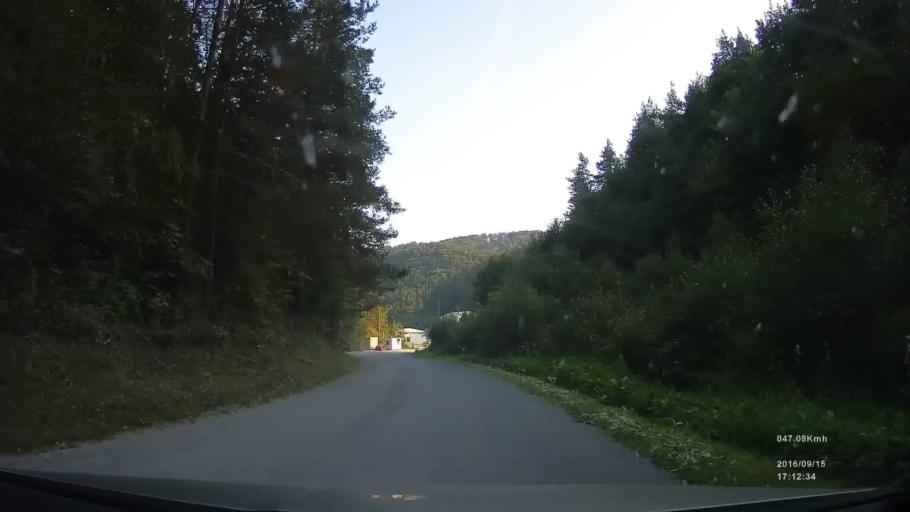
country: SK
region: Presovsky
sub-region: Okres Presov
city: Presov
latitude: 48.9119
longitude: 21.0958
